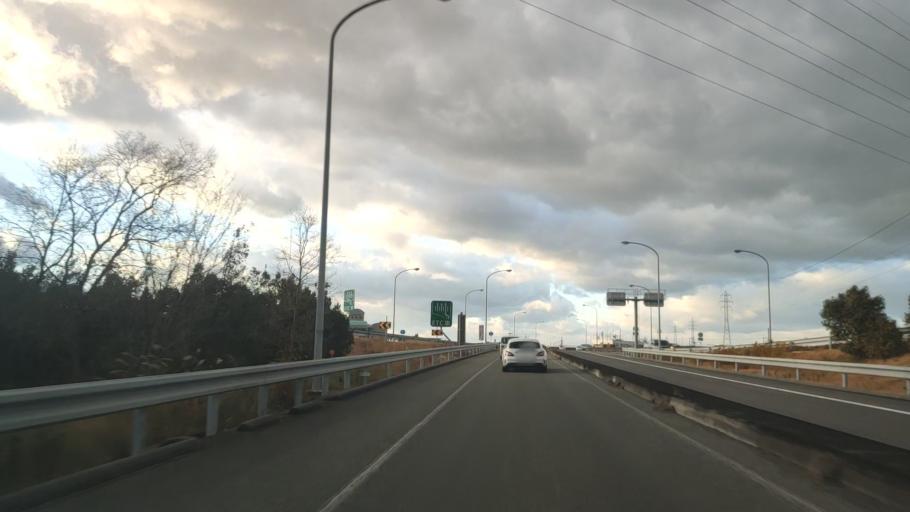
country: JP
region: Ehime
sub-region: Shikoku-chuo Shi
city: Matsuyama
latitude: 33.7952
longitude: 132.7804
